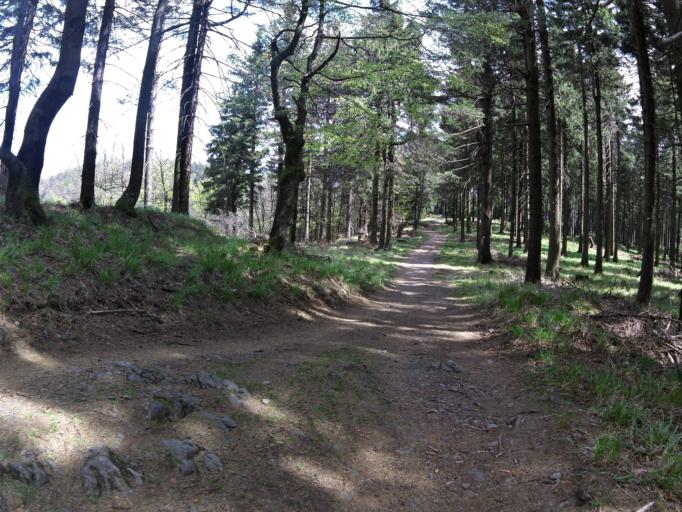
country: DE
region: Thuringia
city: Brotterode
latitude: 50.8454
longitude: 10.4499
